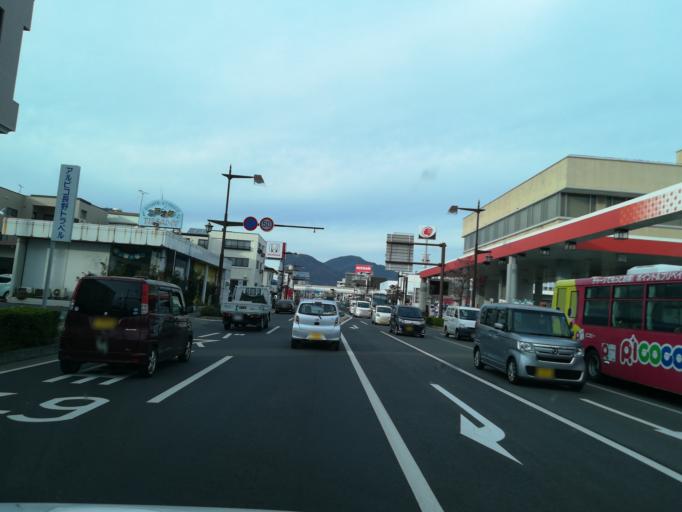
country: JP
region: Nagano
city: Nagano-shi
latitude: 36.6306
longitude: 138.1829
